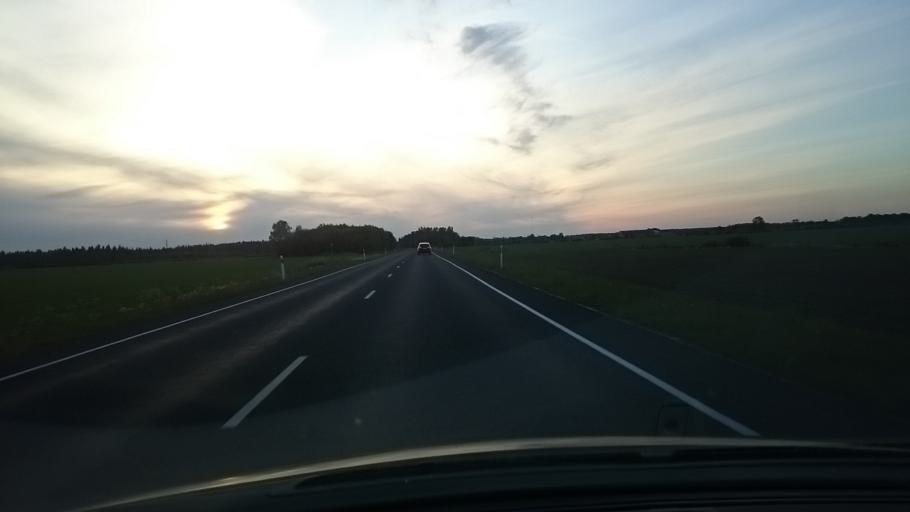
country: EE
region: Viljandimaa
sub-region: Vohma linn
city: Vohma
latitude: 58.7325
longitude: 25.5924
